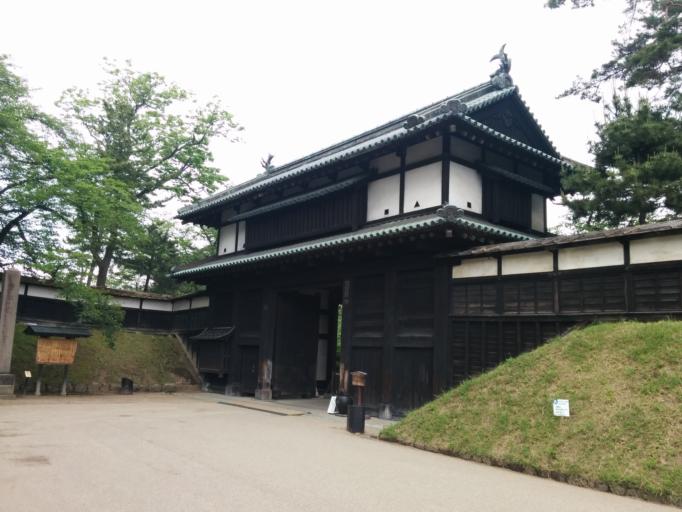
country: JP
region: Aomori
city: Hirosaki
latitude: 40.6036
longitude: 140.4644
